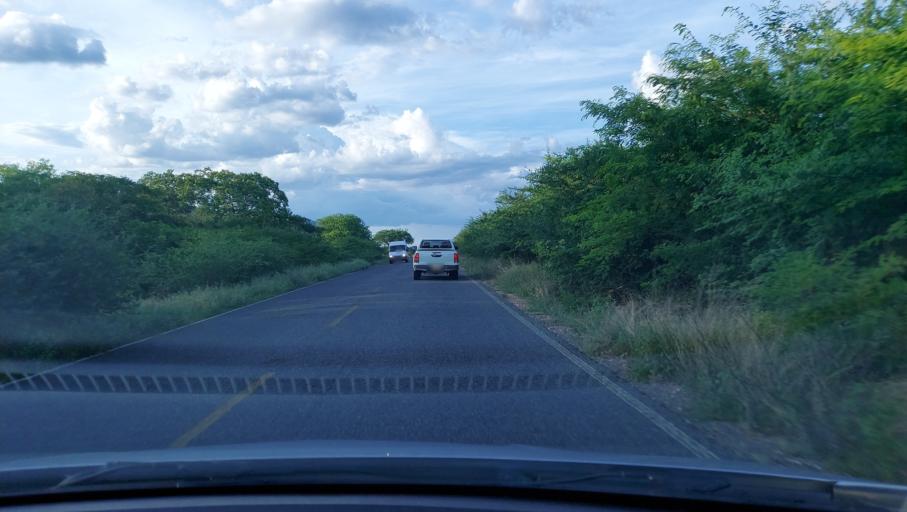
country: BR
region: Bahia
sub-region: Oliveira Dos Brejinhos
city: Beira Rio
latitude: -12.1885
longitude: -42.5389
